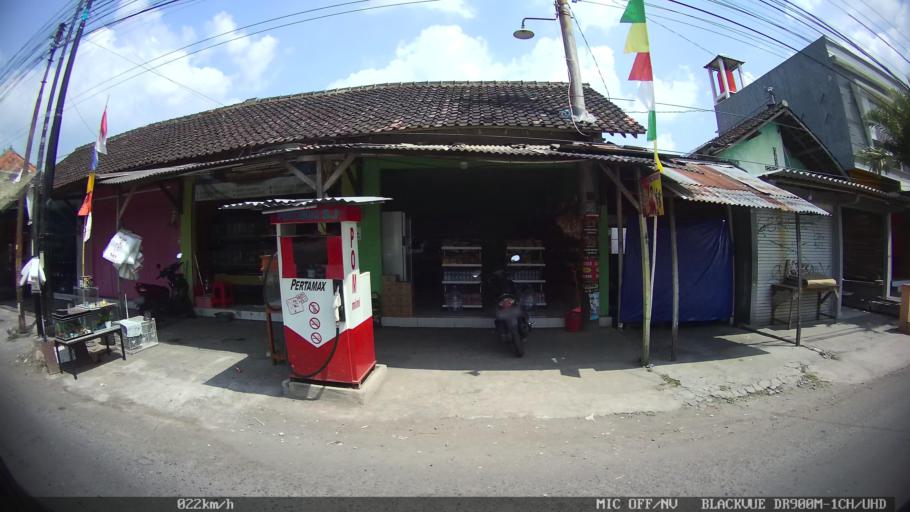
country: ID
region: Daerah Istimewa Yogyakarta
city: Yogyakarta
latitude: -7.8282
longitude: 110.4065
